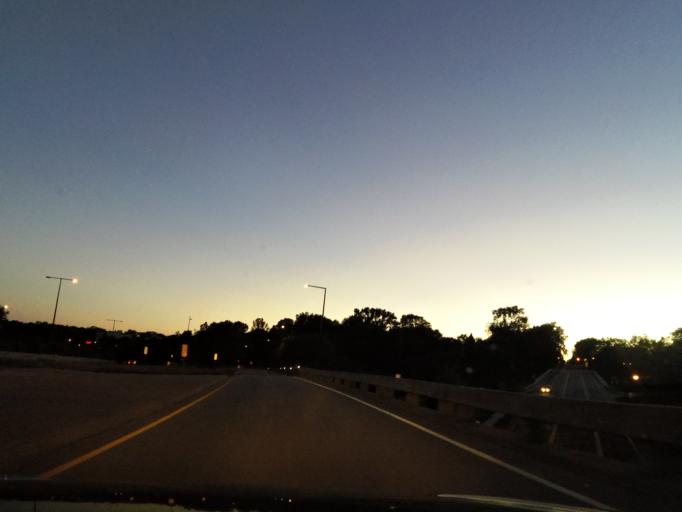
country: US
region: Minnesota
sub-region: Dakota County
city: West Saint Paul
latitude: 44.9307
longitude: -93.1419
